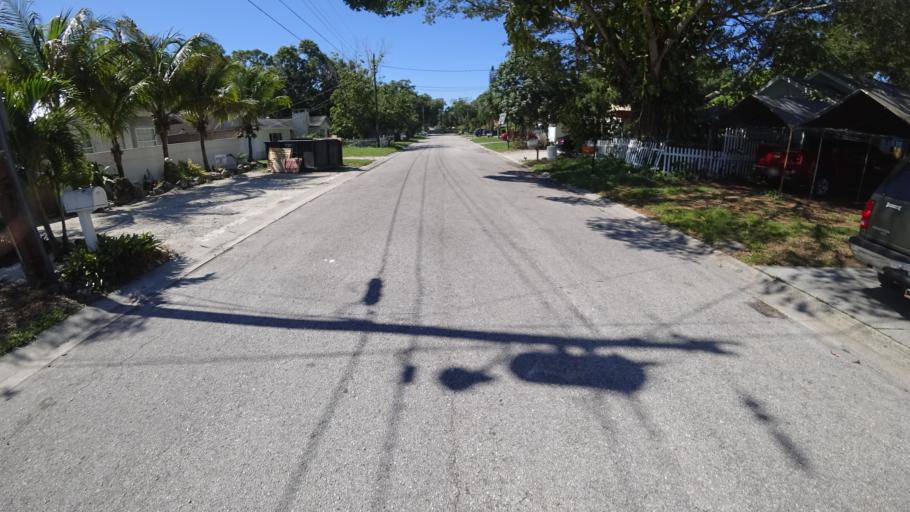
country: US
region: Florida
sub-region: Manatee County
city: West Bradenton
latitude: 27.4897
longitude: -82.5980
